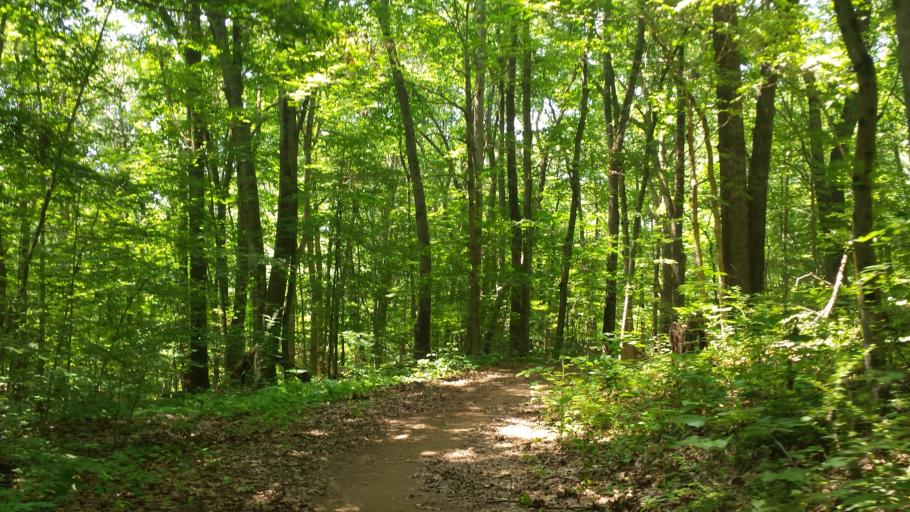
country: US
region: New York
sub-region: Westchester County
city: Yorktown Heights
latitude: 41.2218
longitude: -73.7823
